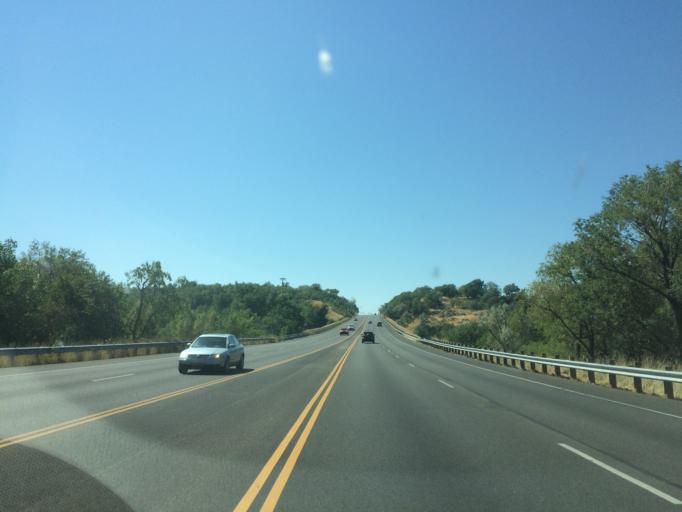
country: US
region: Utah
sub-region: Weber County
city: Ogden
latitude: 41.2380
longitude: -111.9459
